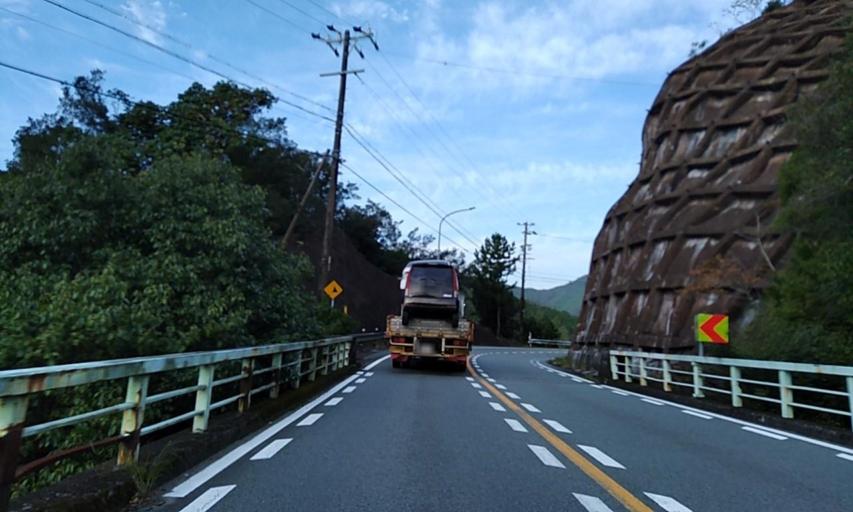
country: JP
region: Mie
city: Toba
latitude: 34.4006
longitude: 136.7826
